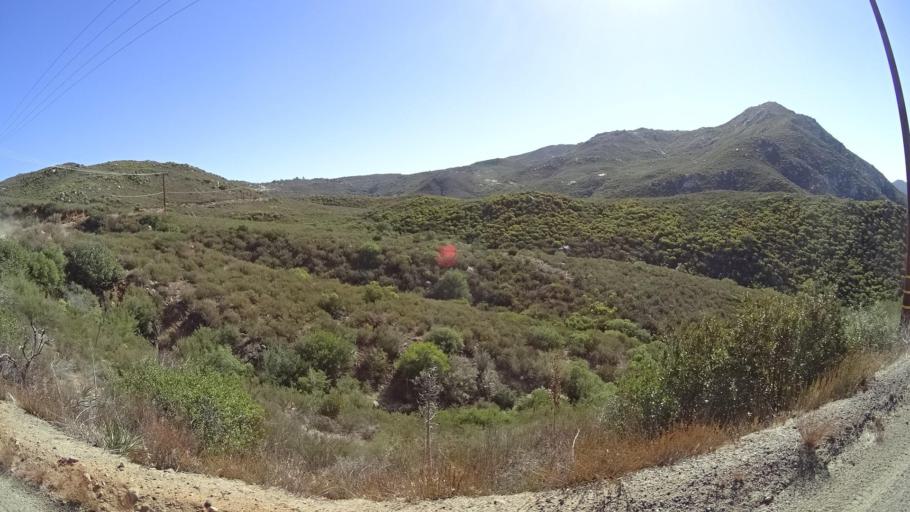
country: US
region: California
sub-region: San Diego County
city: Descanso
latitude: 32.8630
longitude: -116.6689
